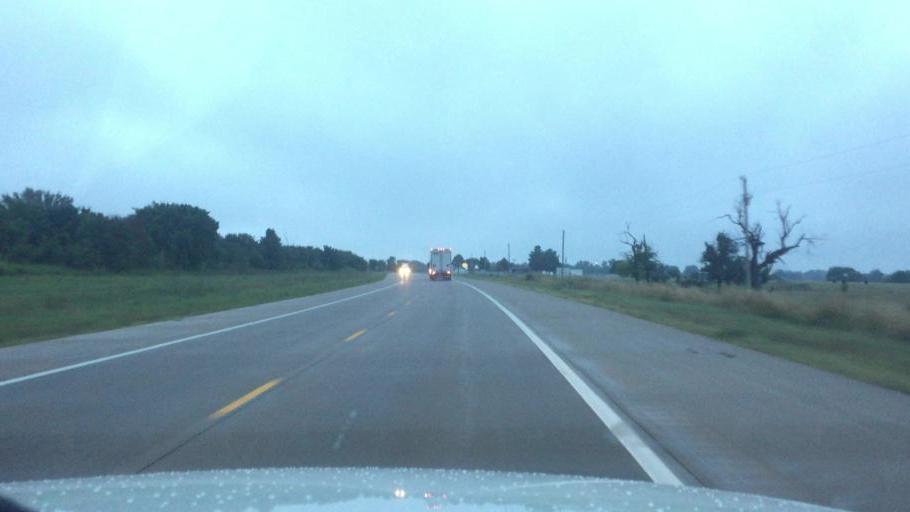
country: US
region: Kansas
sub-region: Neosho County
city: Chanute
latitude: 37.5049
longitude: -95.4708
